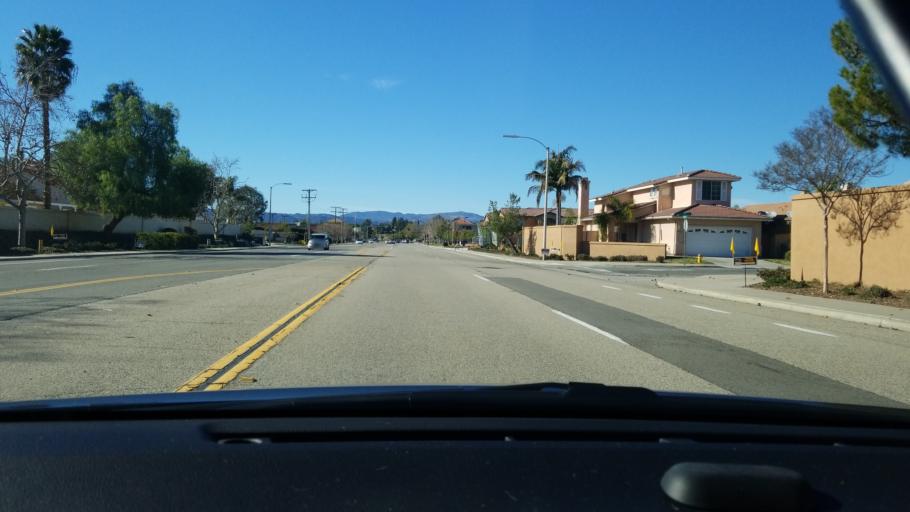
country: US
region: California
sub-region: Riverside County
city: Murrieta Hot Springs
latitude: 33.5381
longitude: -117.1395
